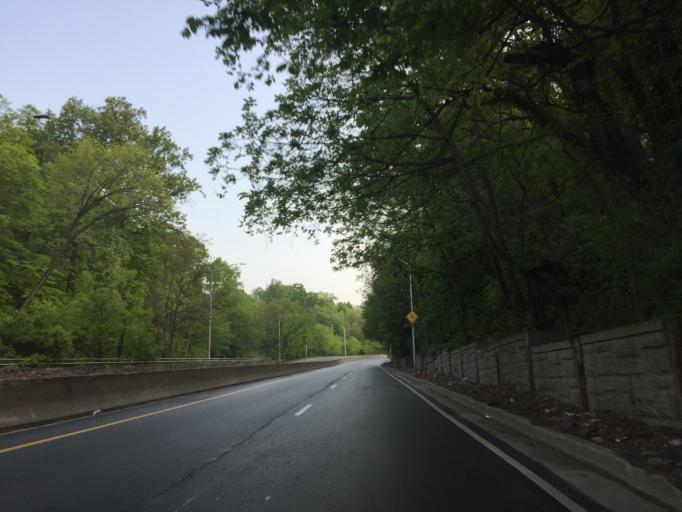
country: US
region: Maryland
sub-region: Baltimore County
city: Charlestown
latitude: 39.3042
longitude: -76.6735
